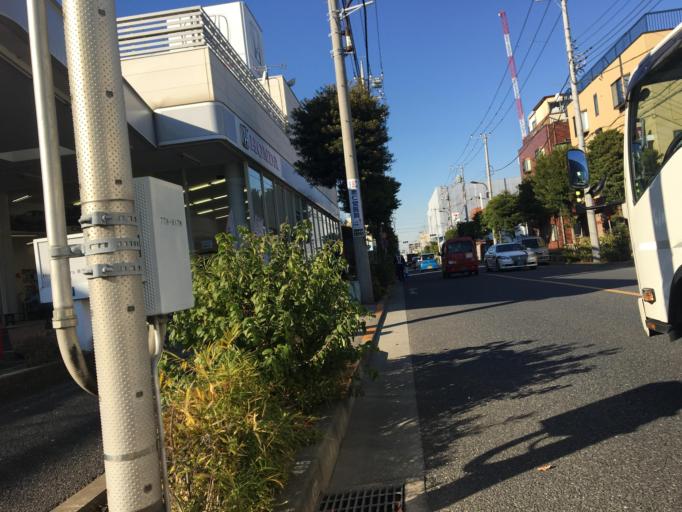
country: JP
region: Tokyo
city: Urayasu
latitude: 35.7194
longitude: 139.8909
